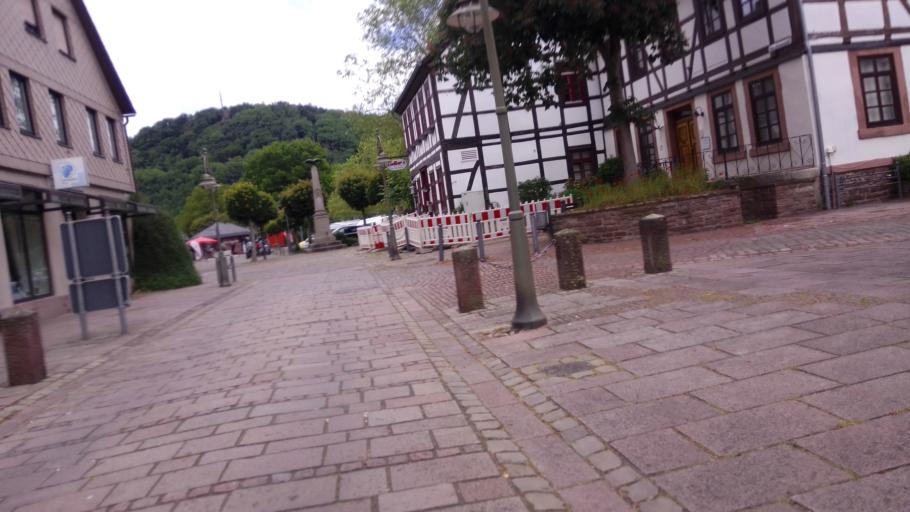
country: DE
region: Lower Saxony
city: Bodenwerder
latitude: 51.9794
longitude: 9.5176
